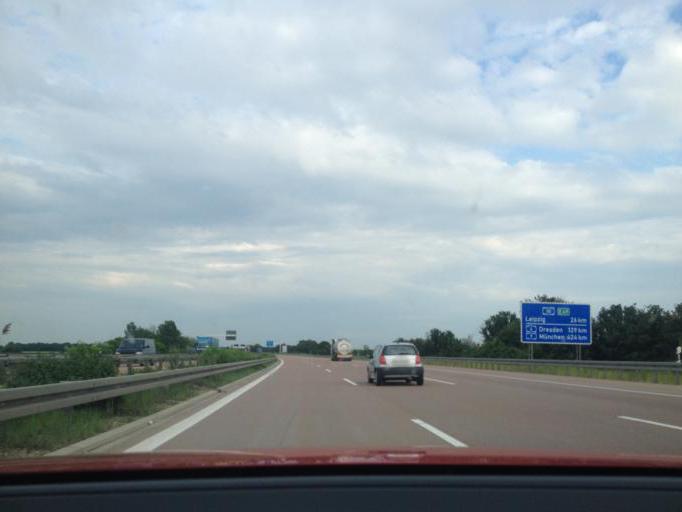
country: DE
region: Saxony-Anhalt
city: Grosskugel
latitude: 51.4357
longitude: 12.1550
